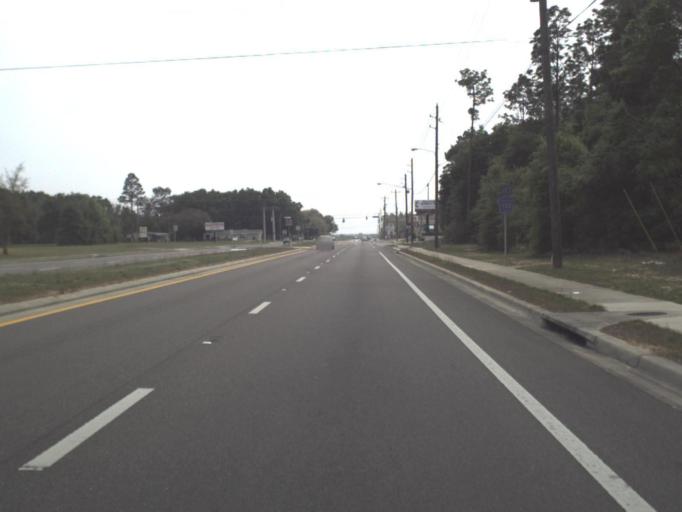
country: US
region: Florida
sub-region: Santa Rosa County
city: Milton
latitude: 30.6483
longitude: -87.0554
